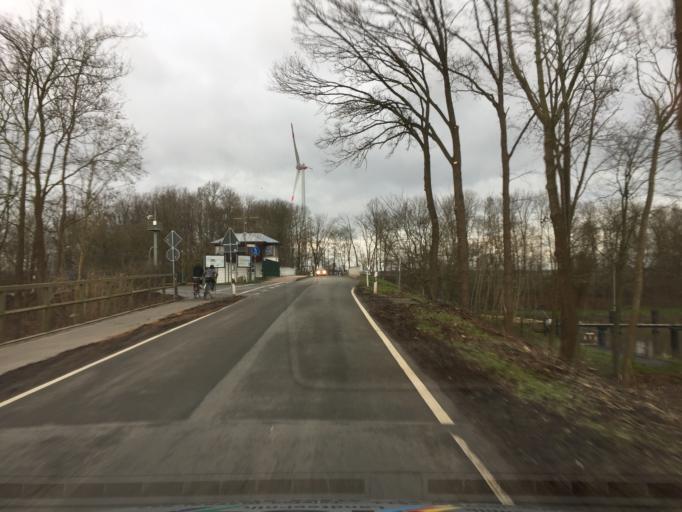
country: DE
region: Lower Saxony
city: Stolzenau
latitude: 52.4942
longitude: 9.0611
